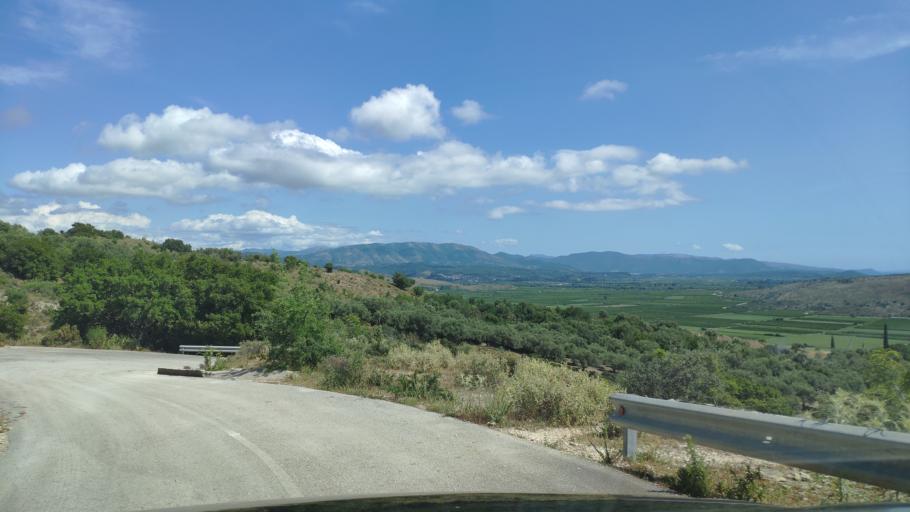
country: AL
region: Vlore
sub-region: Rrethi i Sarandes
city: Konispol
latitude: 39.6260
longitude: 20.2079
